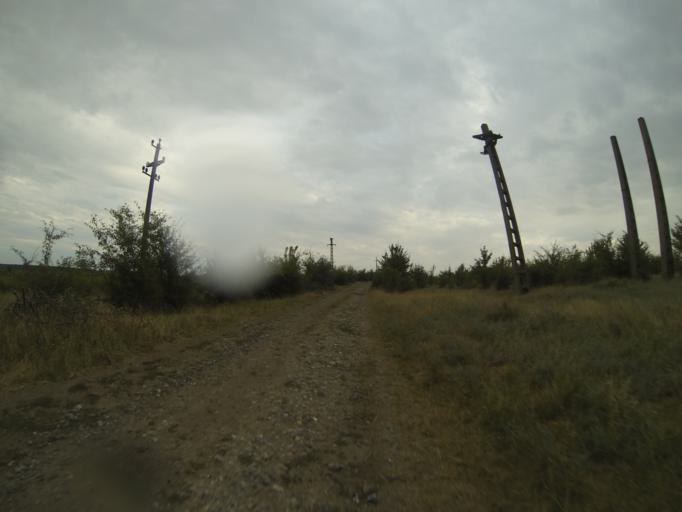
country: RO
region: Dolj
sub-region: Comuna Bradesti
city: Bradesti
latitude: 44.5129
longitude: 23.6658
